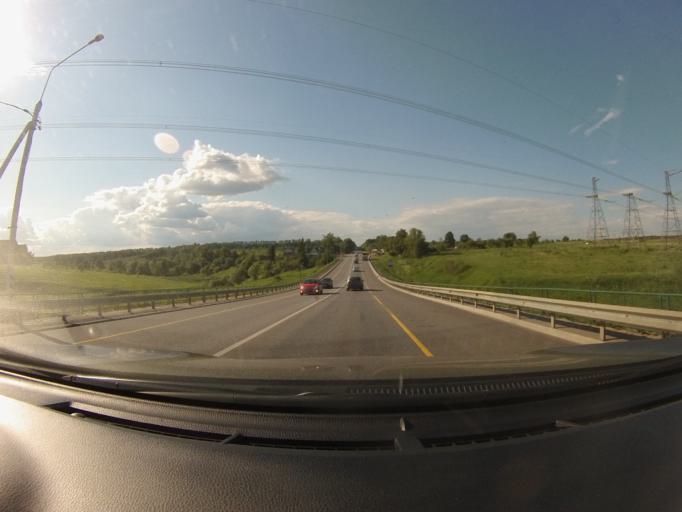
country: RU
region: Tula
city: Barsuki
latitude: 54.3493
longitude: 37.5391
